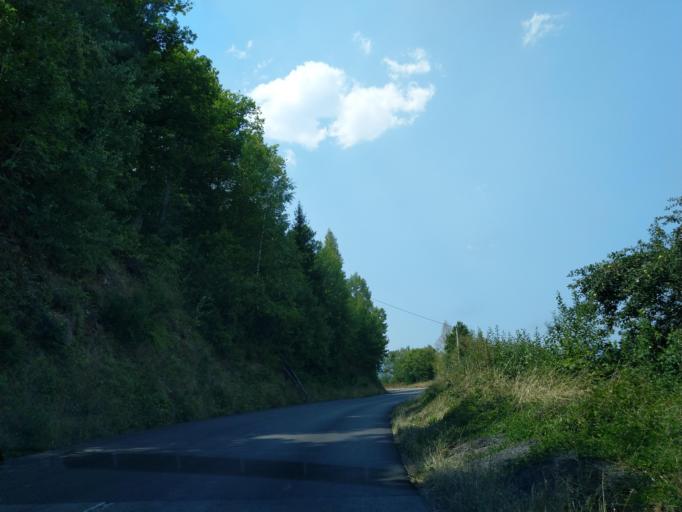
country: RS
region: Central Serbia
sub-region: Zlatiborski Okrug
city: Prijepolje
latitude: 43.3619
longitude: 19.6056
